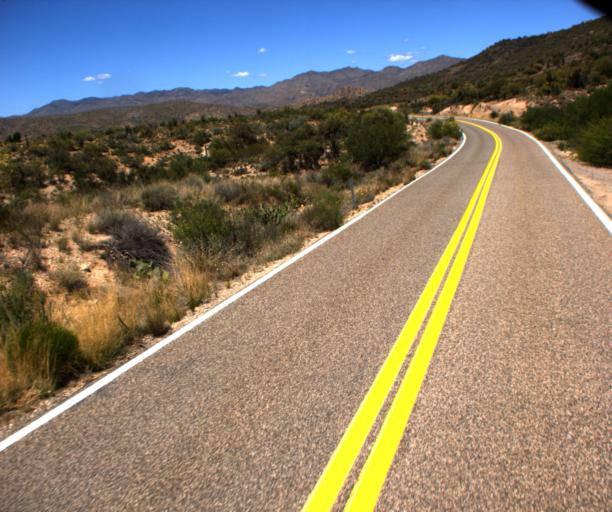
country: US
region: Arizona
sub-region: Yavapai County
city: Bagdad
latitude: 34.5128
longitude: -113.0762
